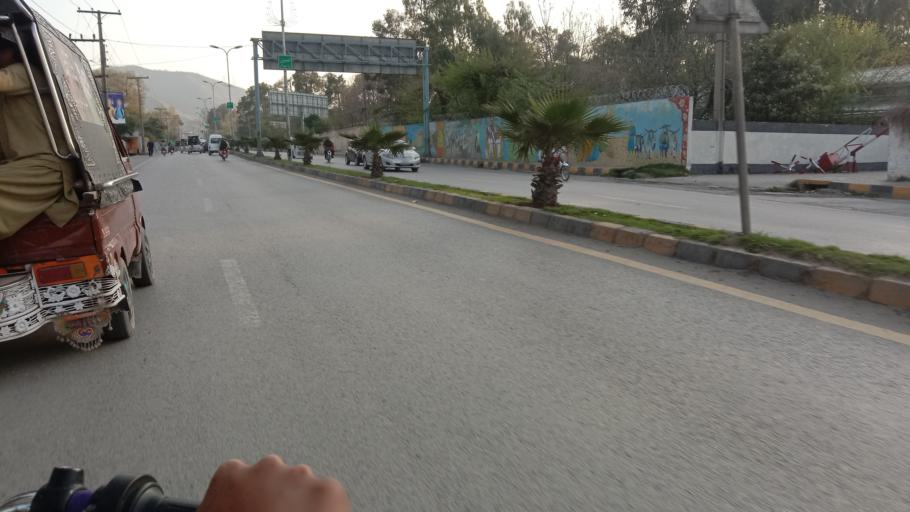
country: PK
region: Khyber Pakhtunkhwa
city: Abbottabad
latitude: 34.1639
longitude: 73.2228
